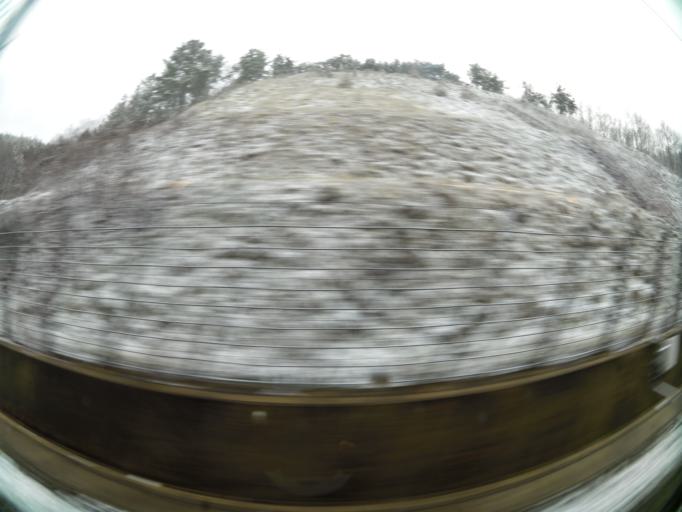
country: KR
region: Chungcheongbuk-do
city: Yong-dong
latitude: 36.1455
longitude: 127.8900
